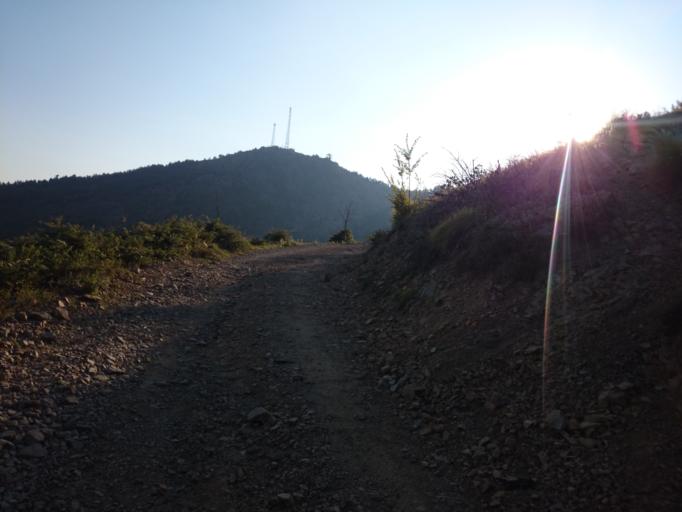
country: AL
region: Lezhe
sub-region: Rrethi i Mirdites
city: Orosh
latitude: 41.8669
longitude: 20.0869
